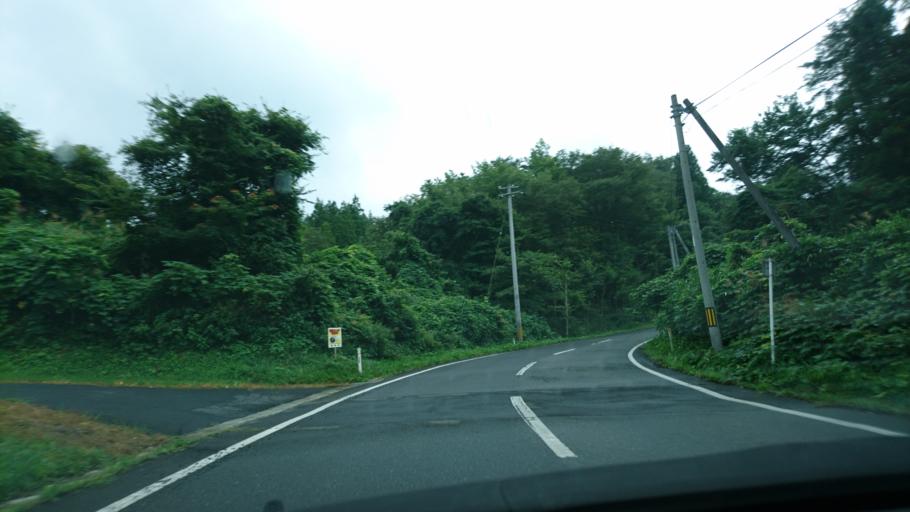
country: JP
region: Iwate
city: Ichinoseki
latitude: 38.8908
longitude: 140.9617
